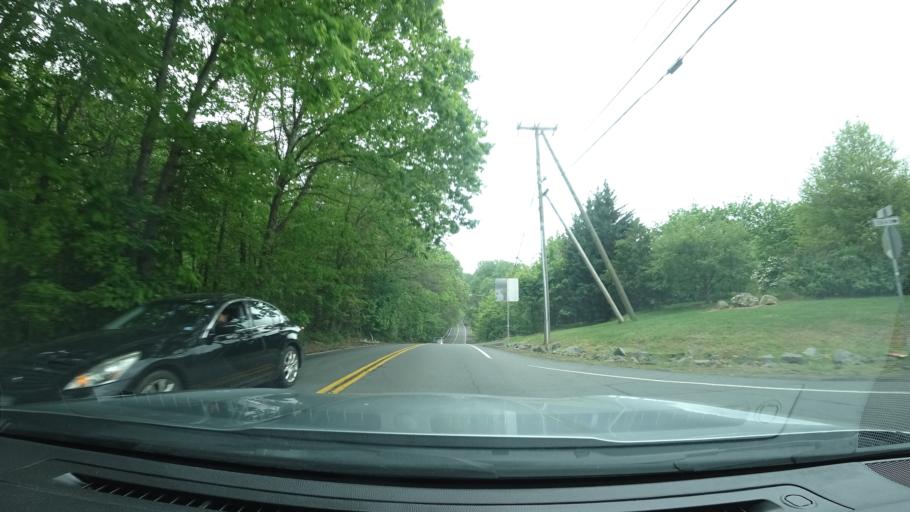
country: US
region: Virginia
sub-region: Fairfax County
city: Oak Hill
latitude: 38.9099
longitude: -77.3618
